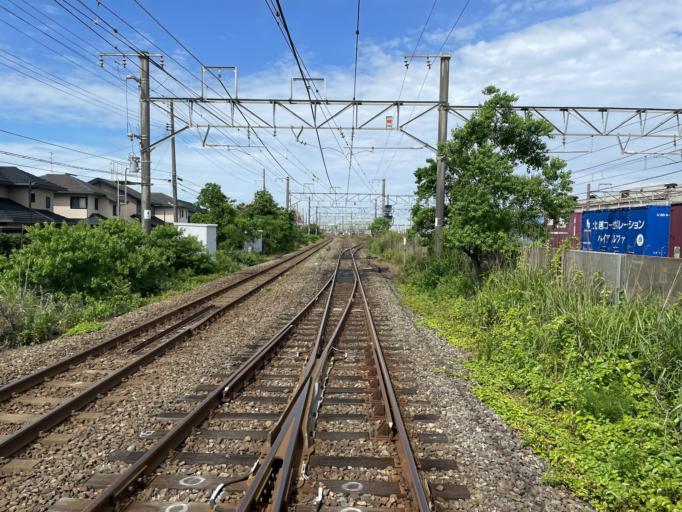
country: JP
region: Niigata
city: Kameda-honcho
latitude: 37.9111
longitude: 139.1147
